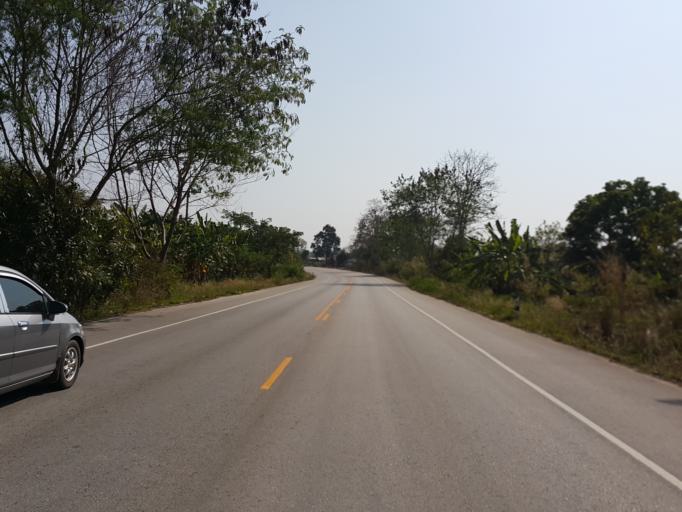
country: TH
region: Lampang
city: Wang Nuea
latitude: 18.9743
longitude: 99.6099
